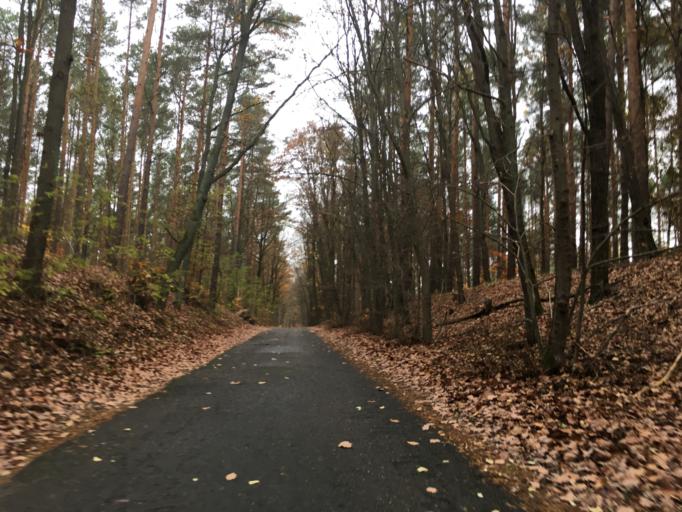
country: DE
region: Brandenburg
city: Mixdorf
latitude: 52.1715
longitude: 14.4407
